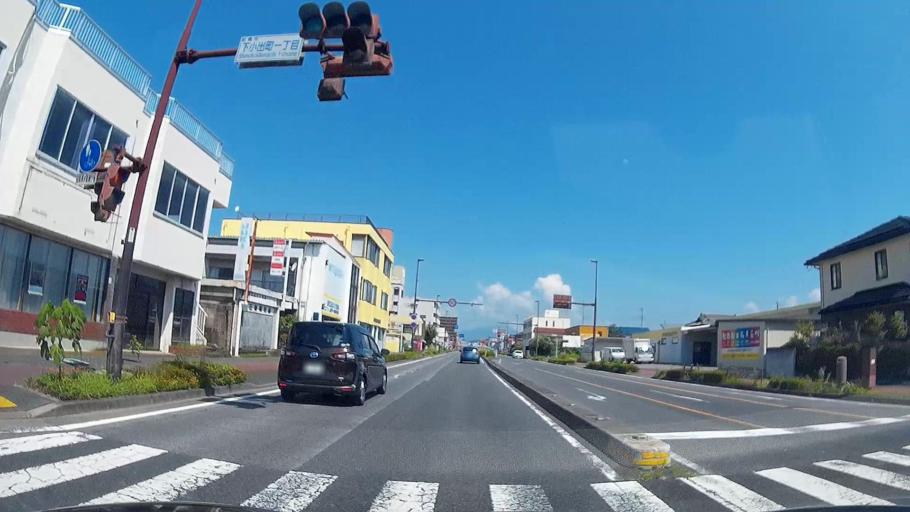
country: JP
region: Gunma
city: Maebashi-shi
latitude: 36.4096
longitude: 139.0647
